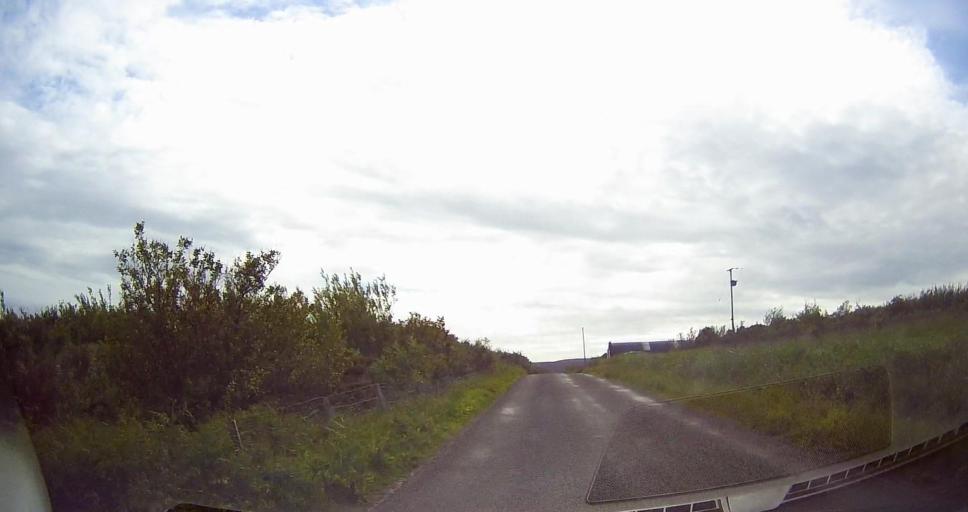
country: GB
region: Scotland
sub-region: Orkney Islands
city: Stromness
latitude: 58.8042
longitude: -3.2210
